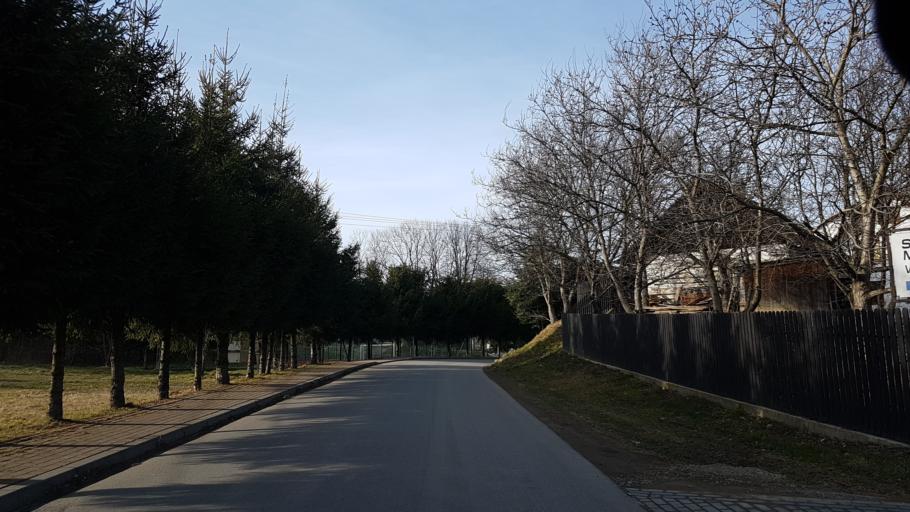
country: PL
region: Lesser Poland Voivodeship
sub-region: Powiat nowosadecki
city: Stary Sacz
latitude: 49.5457
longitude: 20.6259
